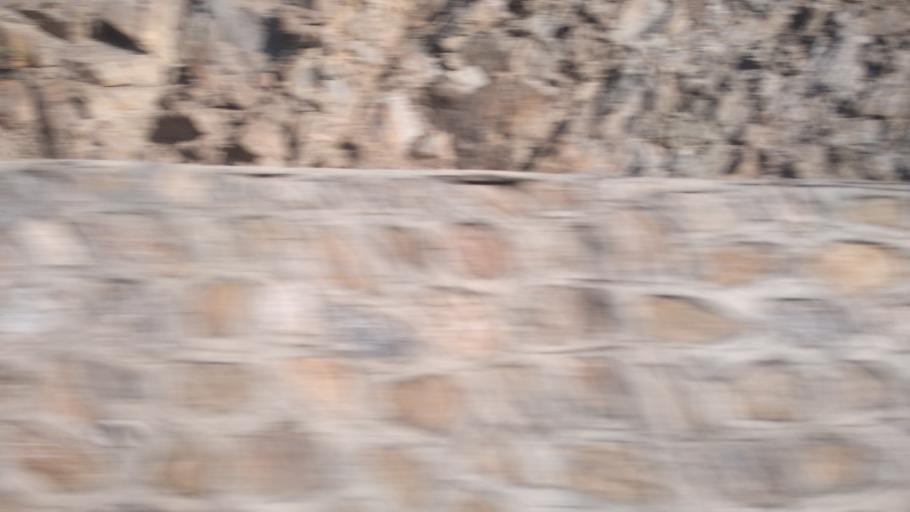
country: TR
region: Bitlis
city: Resadiye
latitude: 38.4758
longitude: 42.5292
